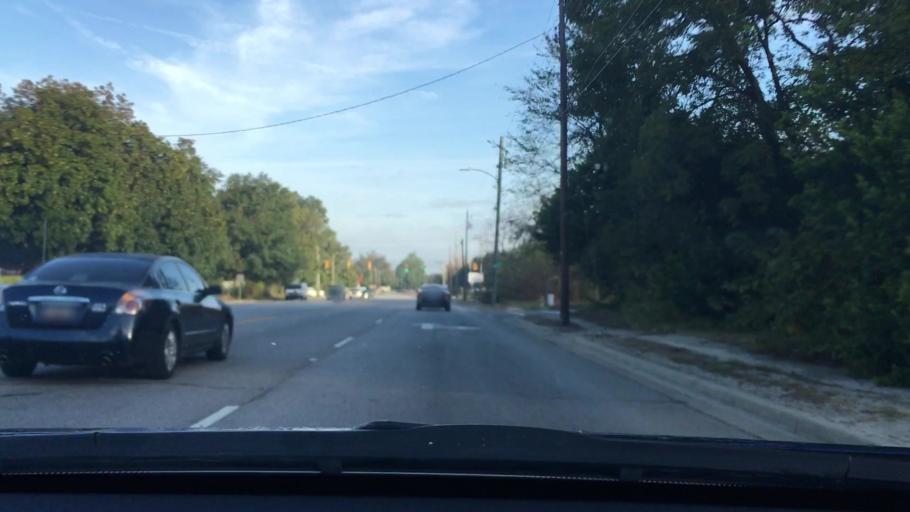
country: US
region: South Carolina
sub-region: Sumter County
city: South Sumter
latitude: 33.9075
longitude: -80.3372
